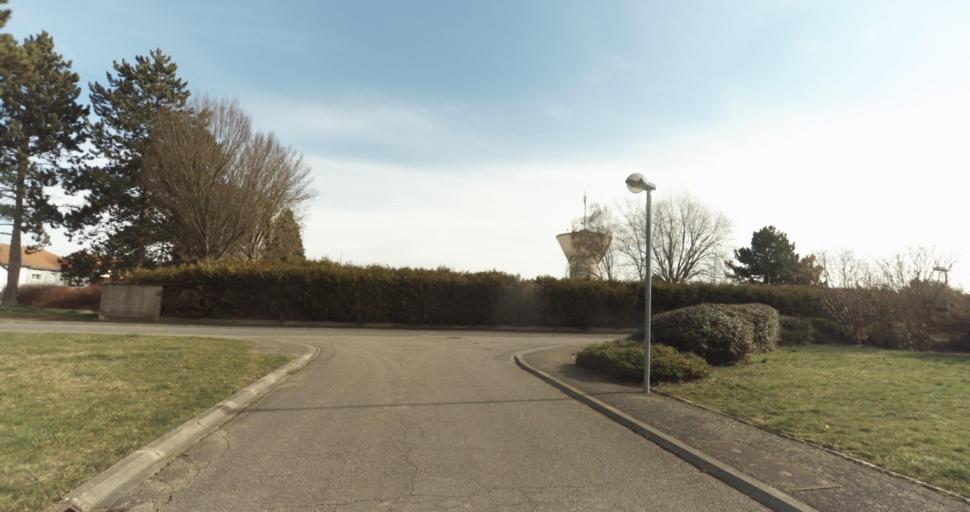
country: FR
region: Lorraine
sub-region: Departement de Meurthe-et-Moselle
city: Jarny
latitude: 49.1516
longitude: 5.8795
